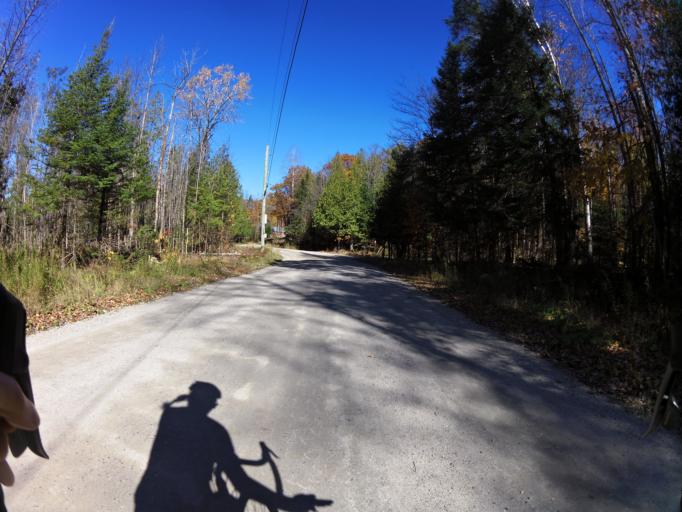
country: CA
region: Quebec
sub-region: Outaouais
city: Wakefield
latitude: 45.7693
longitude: -75.9766
